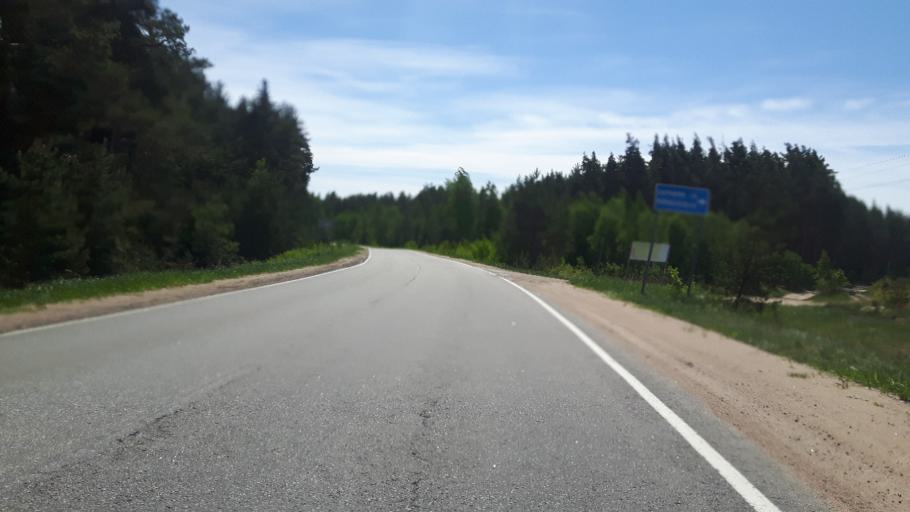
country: EE
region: Ida-Virumaa
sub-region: Narva-Joesuu linn
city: Narva-Joesuu
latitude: 59.5687
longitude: 28.1523
